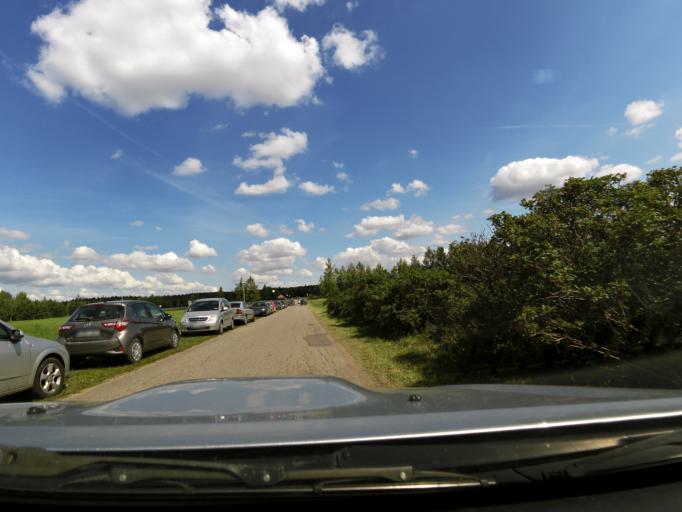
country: LT
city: Birstonas
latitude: 54.6062
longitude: 24.0086
